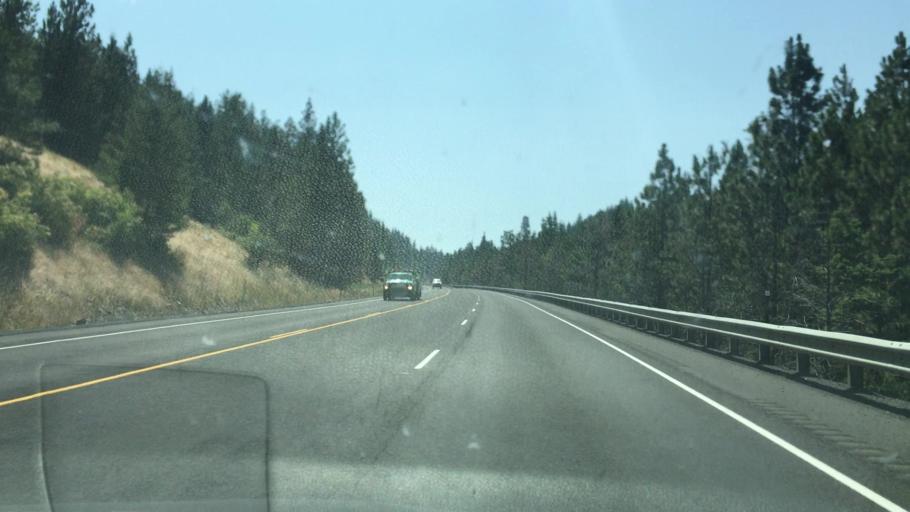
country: US
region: Idaho
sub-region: Idaho County
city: Grangeville
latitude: 45.8639
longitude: -116.2369
